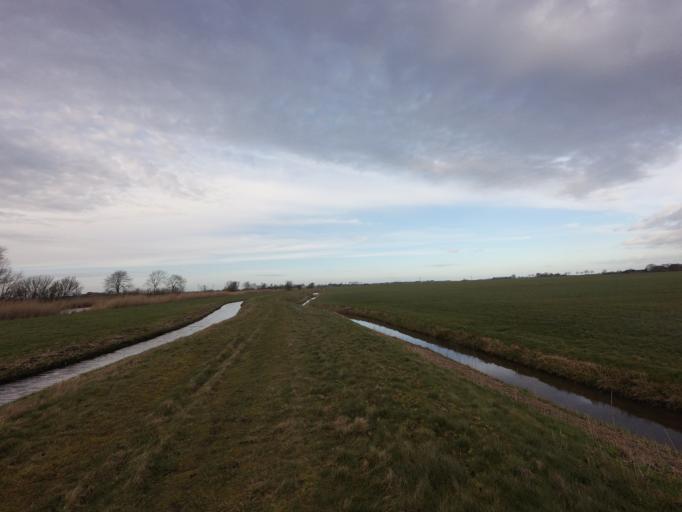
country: NL
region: Friesland
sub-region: Sudwest Fryslan
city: Bolsward
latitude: 53.0290
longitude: 5.4881
